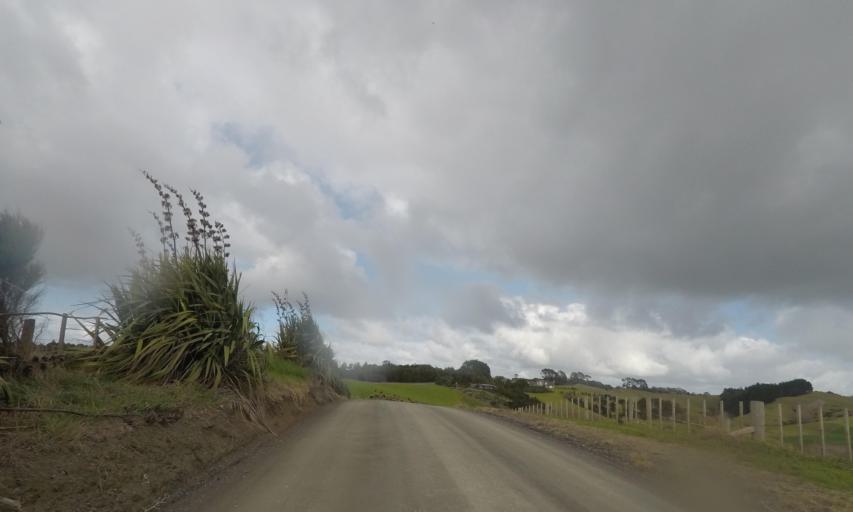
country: NZ
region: Auckland
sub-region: Auckland
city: Wellsford
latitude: -36.1652
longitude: 174.6024
